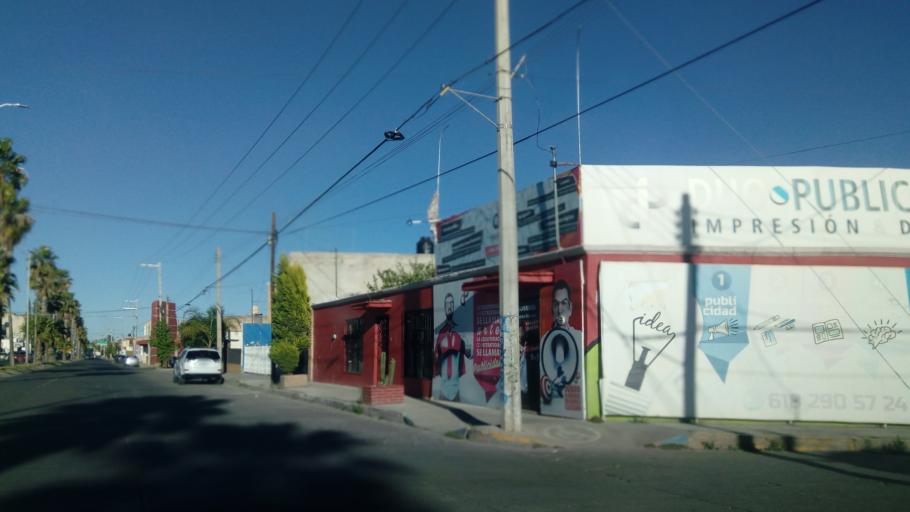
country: MX
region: Durango
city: Victoria de Durango
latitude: 24.0114
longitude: -104.6873
